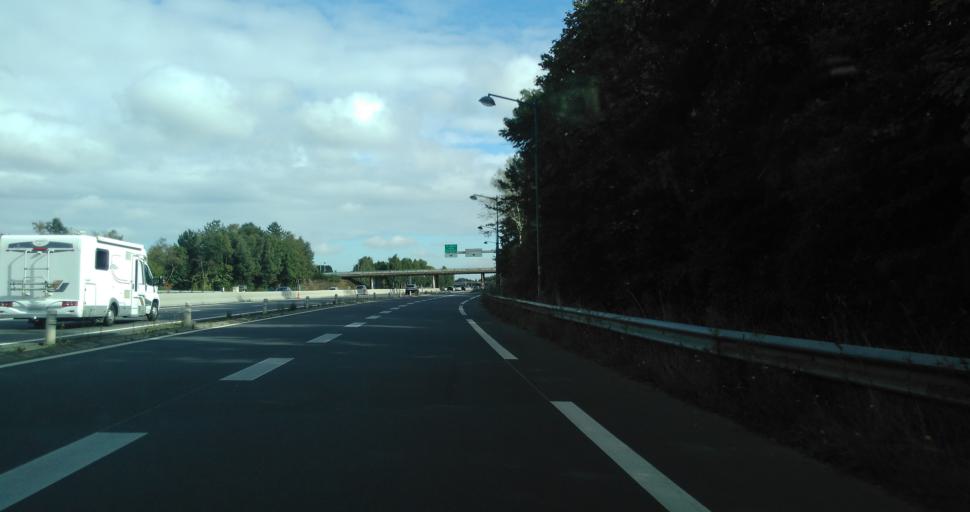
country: FR
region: Brittany
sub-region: Departement d'Ille-et-Vilaine
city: Montgermont
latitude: 48.1230
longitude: -1.7185
